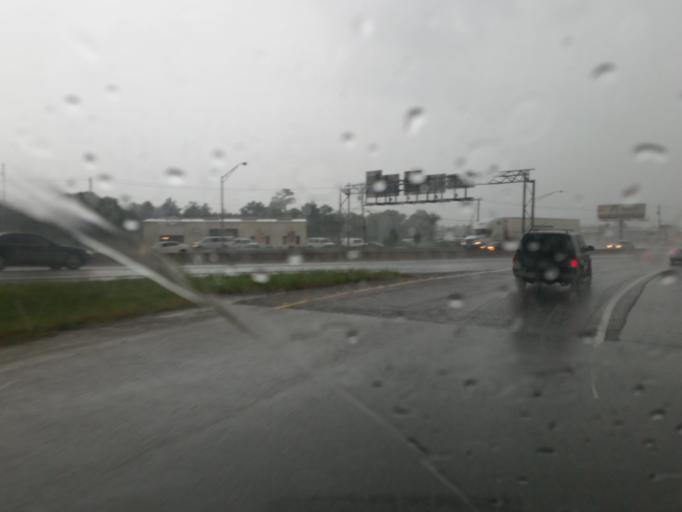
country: US
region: Alabama
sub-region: Mobile County
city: Prichard
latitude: 30.7097
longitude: -88.1215
